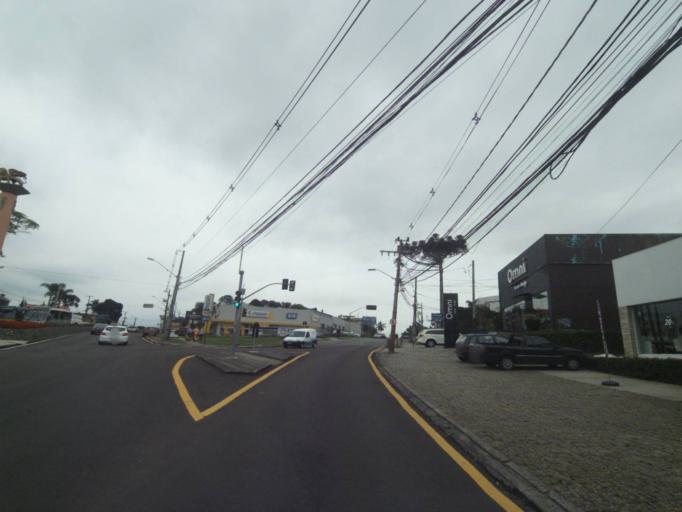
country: BR
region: Parana
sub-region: Curitiba
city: Curitiba
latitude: -25.4180
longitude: -49.2937
